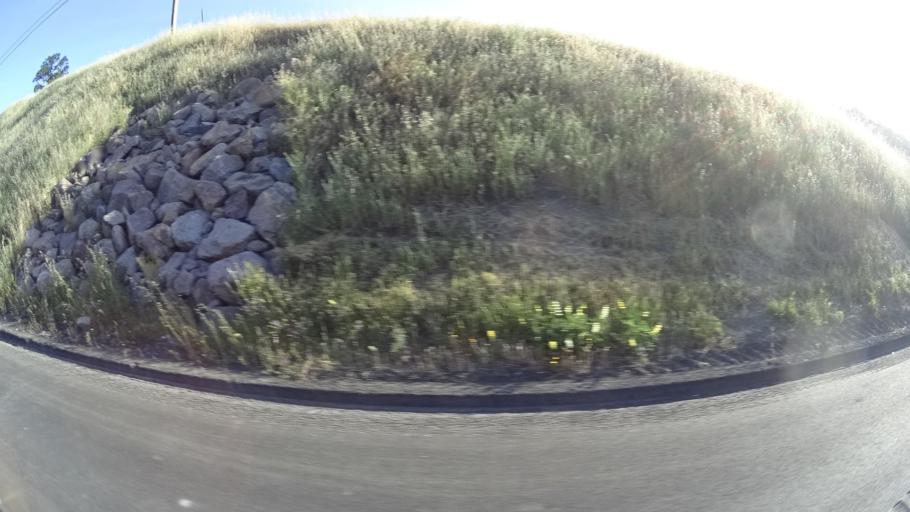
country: US
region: California
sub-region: Lake County
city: Upper Lake
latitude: 39.1744
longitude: -122.9474
